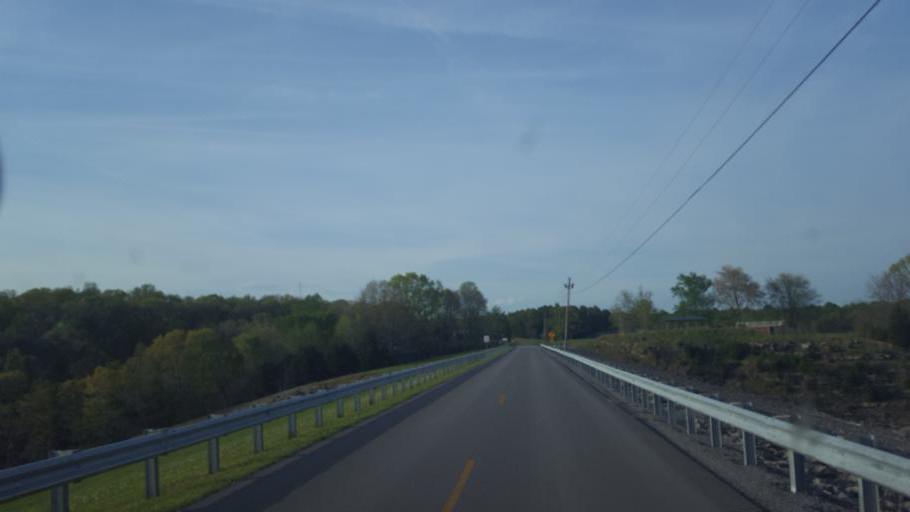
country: US
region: Kentucky
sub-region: Allen County
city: Scottsville
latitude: 36.8948
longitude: -86.1252
